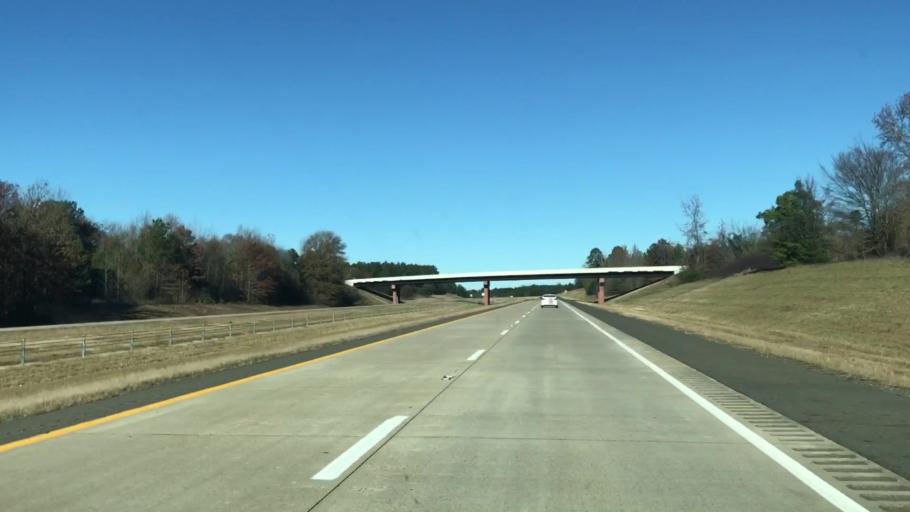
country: US
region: Texas
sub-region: Bowie County
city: Texarkana
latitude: 33.3301
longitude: -93.9584
